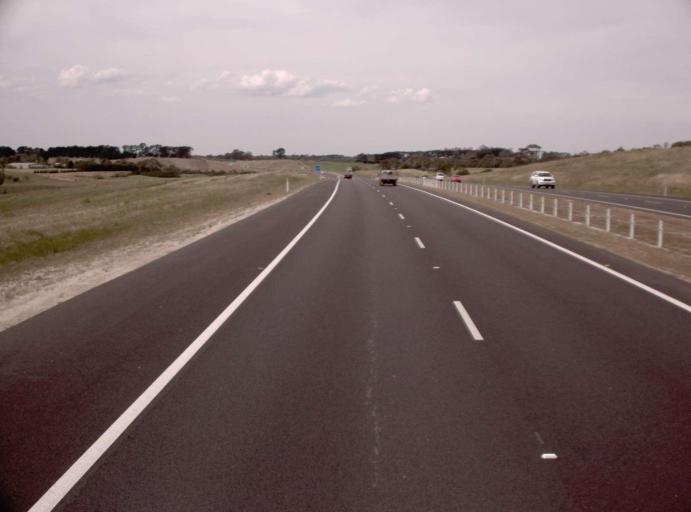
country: AU
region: Victoria
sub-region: Mornington Peninsula
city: Moorooduc
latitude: -38.2703
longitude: 145.0903
